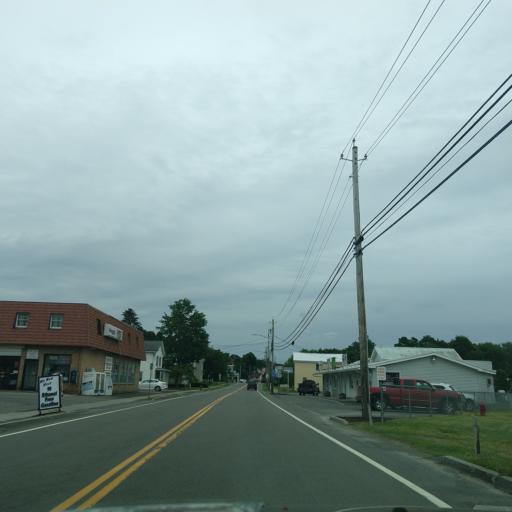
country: US
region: New York
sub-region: Cortland County
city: McGraw
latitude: 42.4439
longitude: -76.0346
